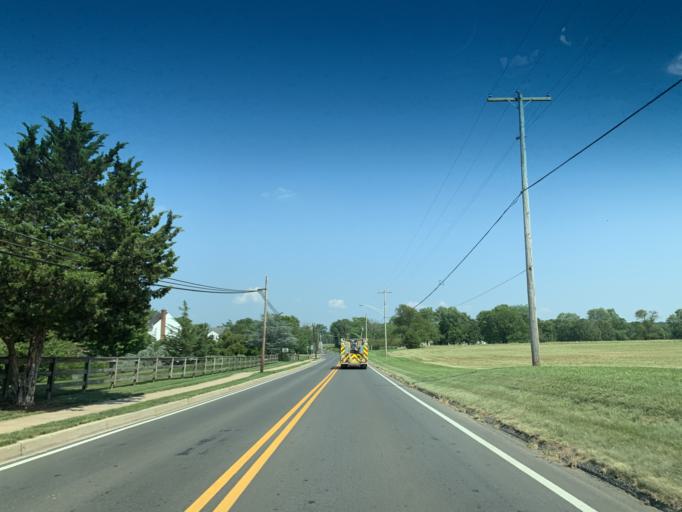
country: US
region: Maryland
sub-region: Montgomery County
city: Poolesville
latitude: 39.1333
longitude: -77.3995
